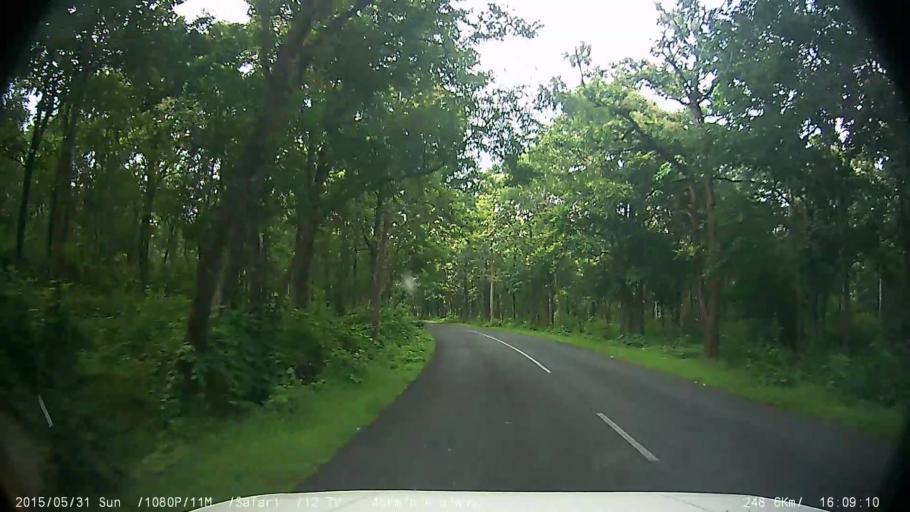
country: IN
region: Karnataka
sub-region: Mysore
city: Sargur
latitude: 11.7258
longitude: 76.4338
